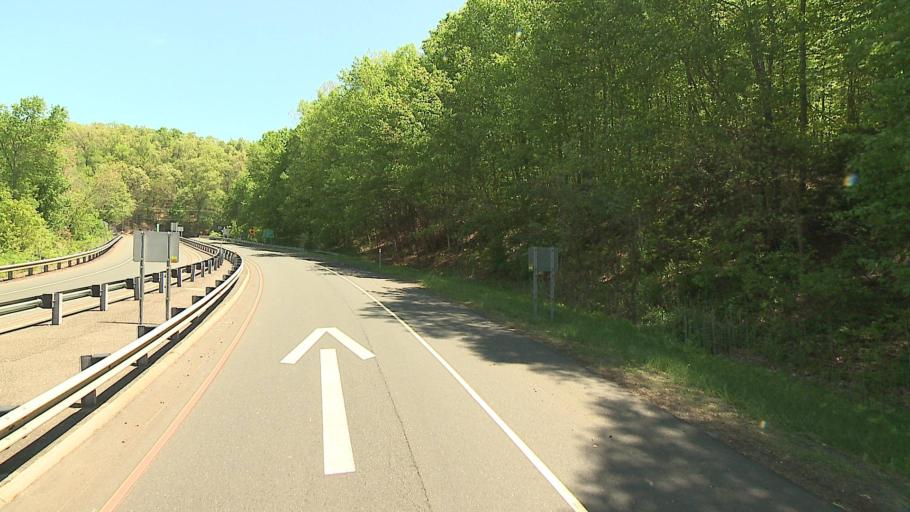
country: US
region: Connecticut
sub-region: New Haven County
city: Heritage Village
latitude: 41.4553
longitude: -73.2347
